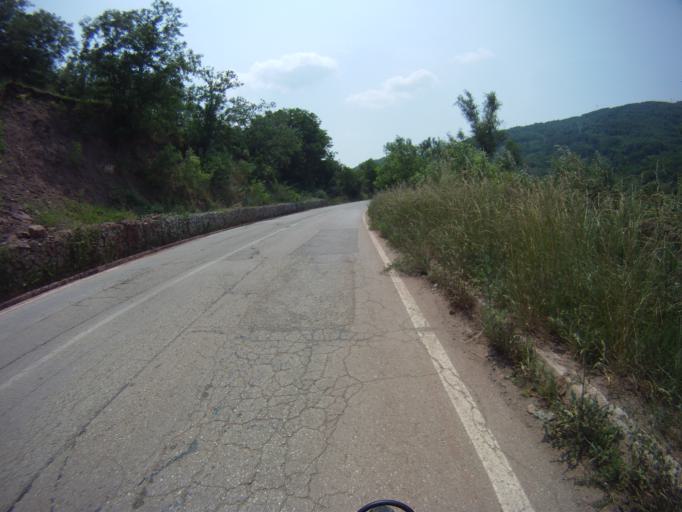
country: RS
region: Central Serbia
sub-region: Nisavski Okrug
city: Gadzin Han
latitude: 43.2420
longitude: 22.0157
